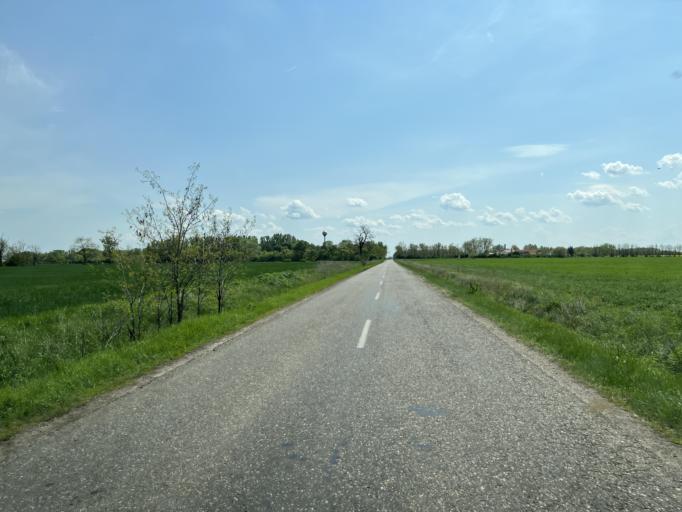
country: HU
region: Pest
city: Tapioszentmarton
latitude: 47.2593
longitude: 19.7725
